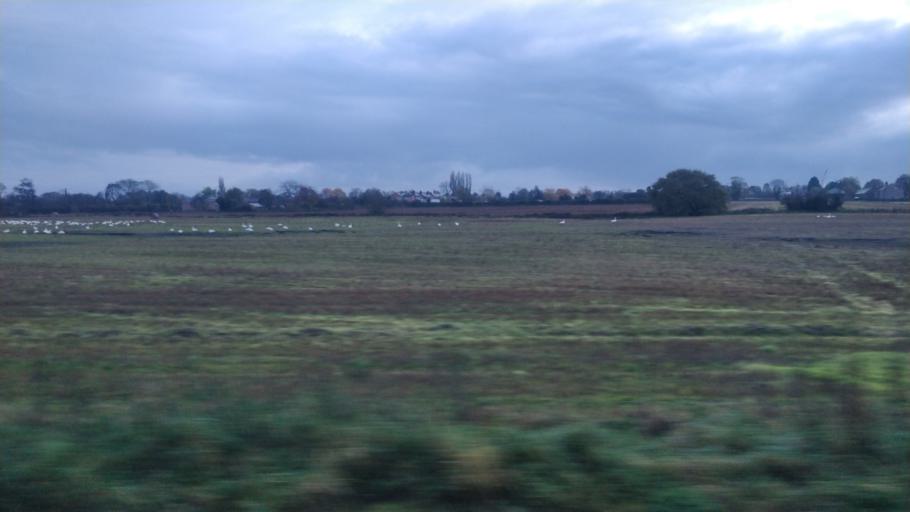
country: GB
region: England
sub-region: Lancashire
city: Ormskirk
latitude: 53.6088
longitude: -2.8567
